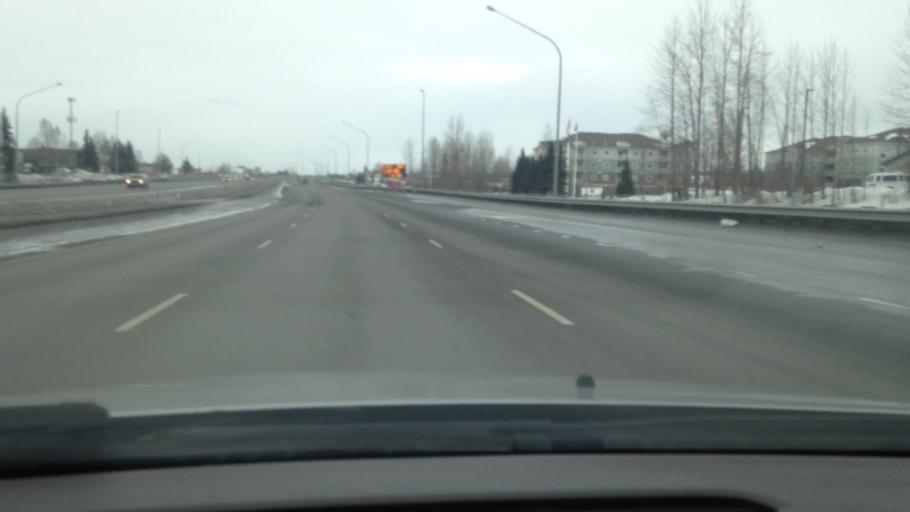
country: US
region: Alaska
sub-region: Anchorage Municipality
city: Anchorage
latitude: 61.1557
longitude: -149.8545
